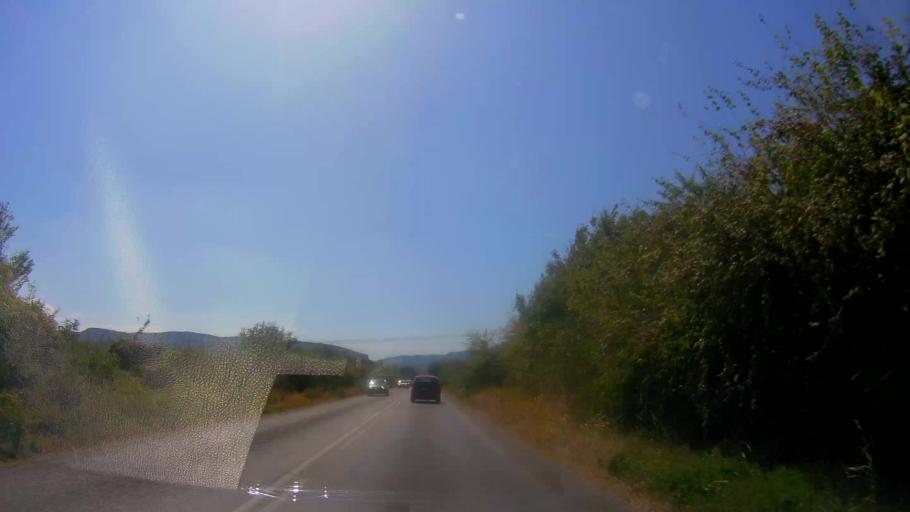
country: BG
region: Veliko Turnovo
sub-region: Obshtina Gorna Oryakhovitsa
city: Purvomaytsi
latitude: 43.1599
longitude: 25.6195
